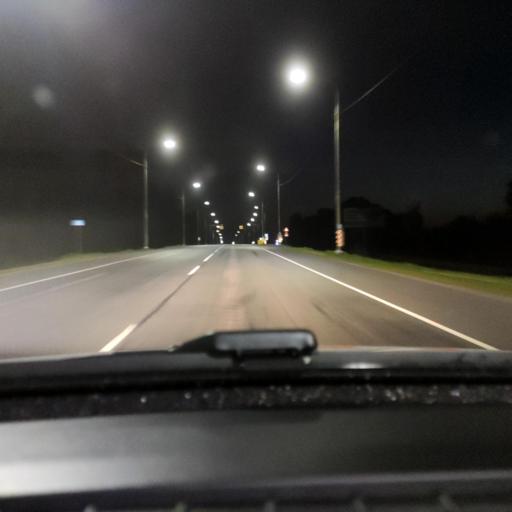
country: RU
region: Voronezj
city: Kashirskoye
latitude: 51.4961
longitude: 39.5958
